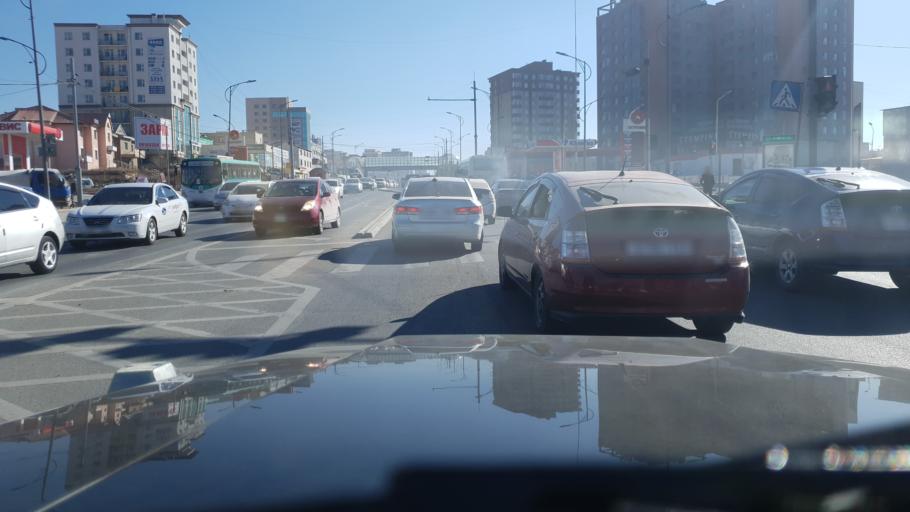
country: MN
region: Ulaanbaatar
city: Ulaanbaatar
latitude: 47.9289
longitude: 106.9355
